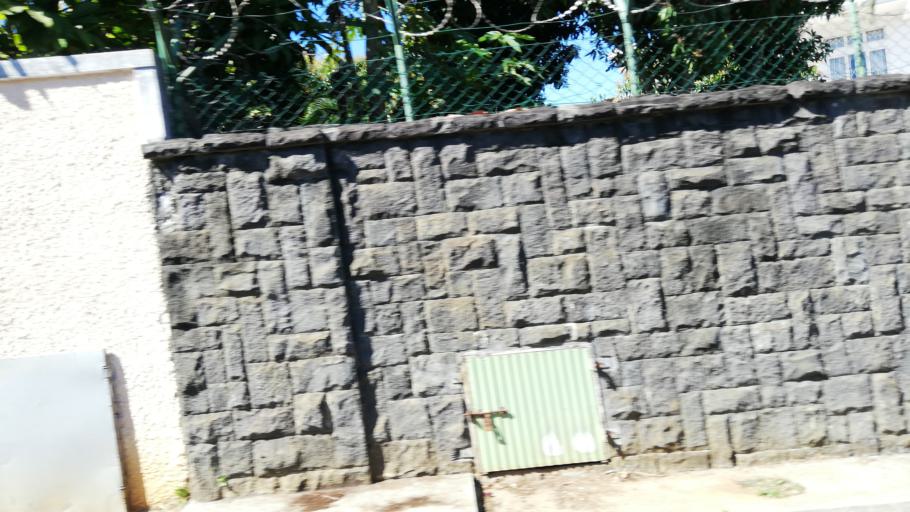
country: MU
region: Plaines Wilhems
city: Ebene
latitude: -20.2338
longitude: 57.4752
